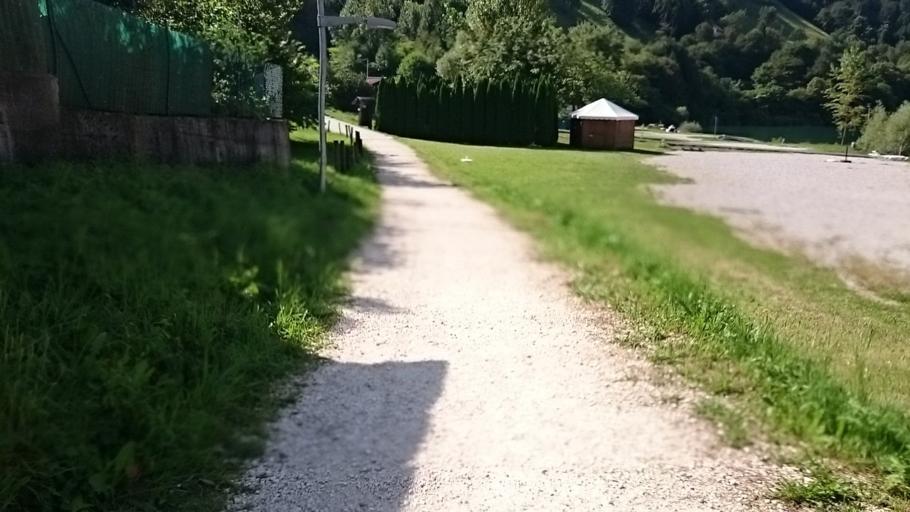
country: IT
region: Veneto
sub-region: Provincia di Belluno
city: Farra d'Alpago
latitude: 46.1068
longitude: 12.3529
